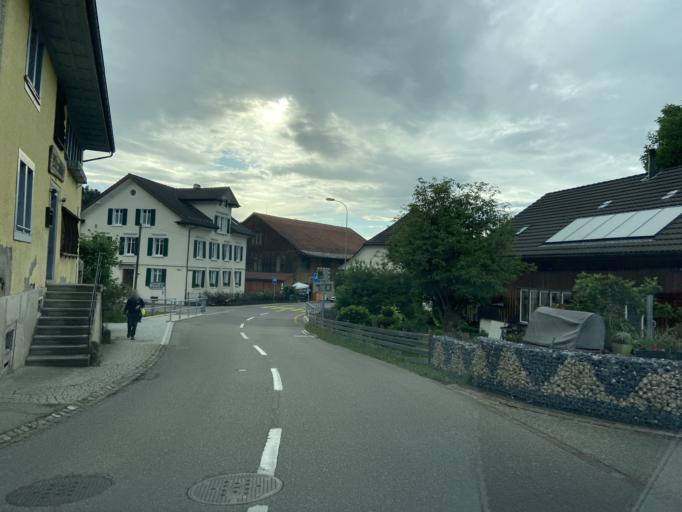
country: CH
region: Zurich
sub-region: Bezirk Winterthur
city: Elgg / Staedtchen und Umgebung
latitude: 47.4924
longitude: 8.8646
